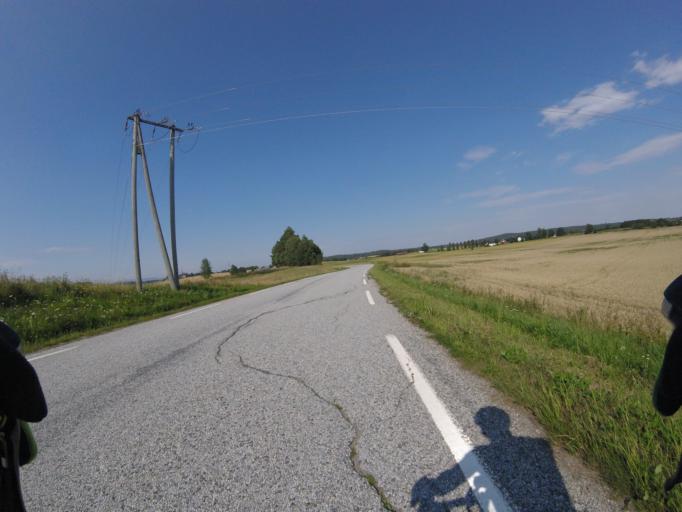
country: NO
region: Akershus
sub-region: Ullensaker
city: Klofta
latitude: 60.0915
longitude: 11.1605
